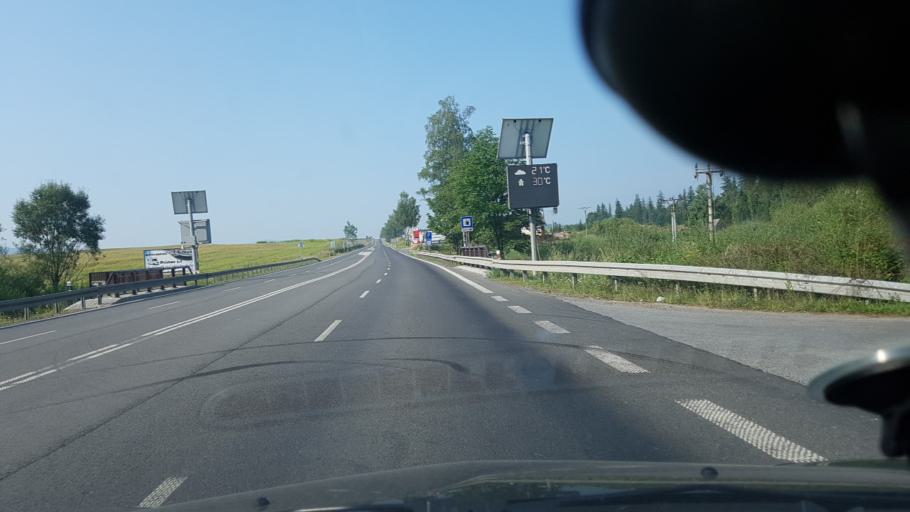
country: PL
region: Lesser Poland Voivodeship
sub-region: Powiat nowotarski
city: Chyzne
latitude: 49.4026
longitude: 19.6531
